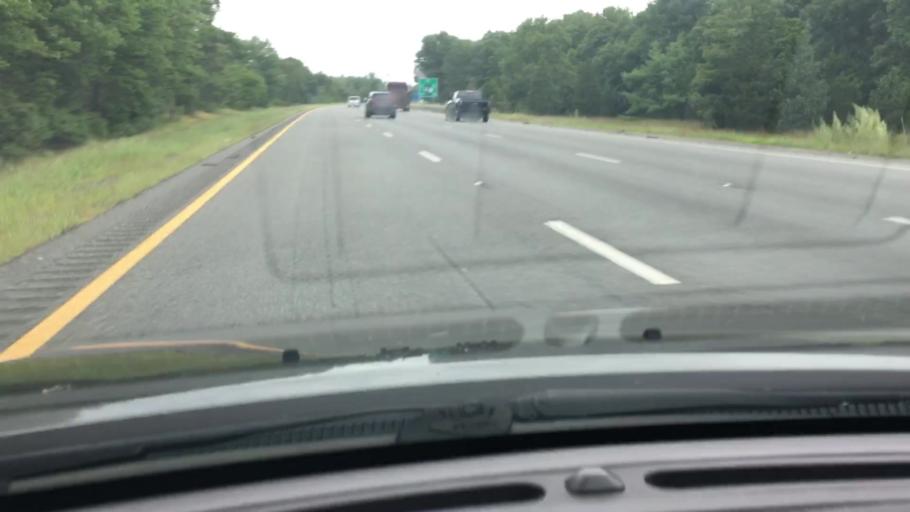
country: US
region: Massachusetts
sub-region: Norfolk County
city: Bellingham
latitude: 42.1164
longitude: -71.4674
